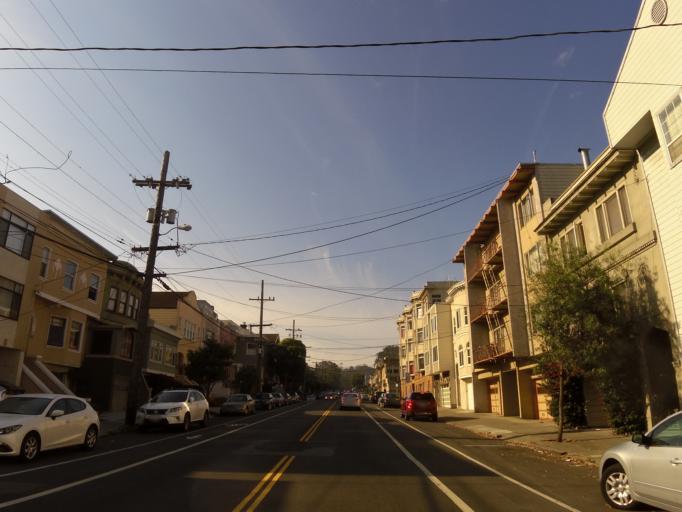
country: US
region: California
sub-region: San Francisco County
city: San Francisco
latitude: 37.7613
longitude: -122.4640
